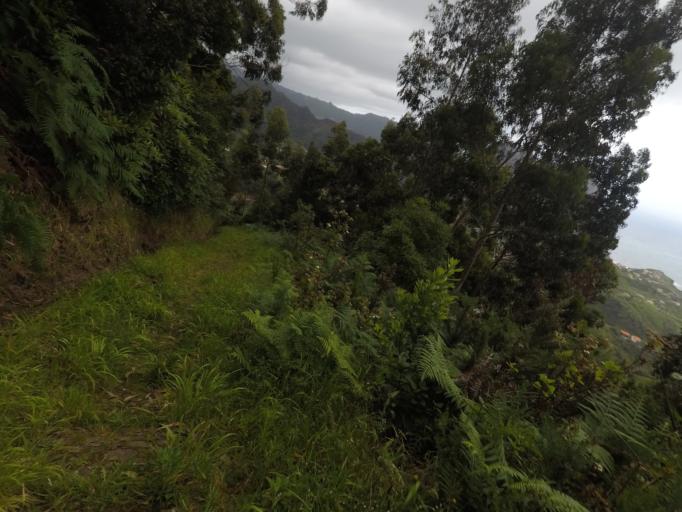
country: PT
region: Madeira
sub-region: Santa Cruz
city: Santa Cruz
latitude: 32.7509
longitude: -16.8254
